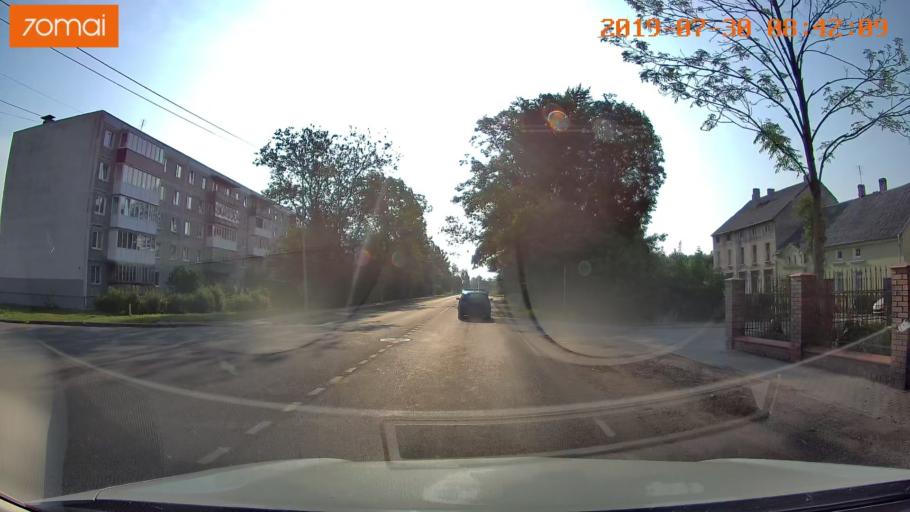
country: RU
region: Kaliningrad
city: Chernyakhovsk
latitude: 54.6298
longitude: 21.8247
